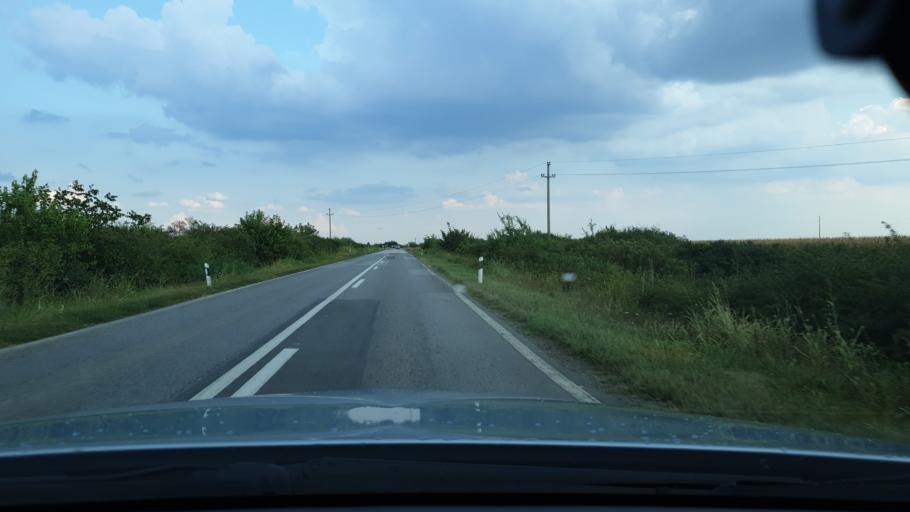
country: RS
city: Boka
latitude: 45.3469
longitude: 20.8167
